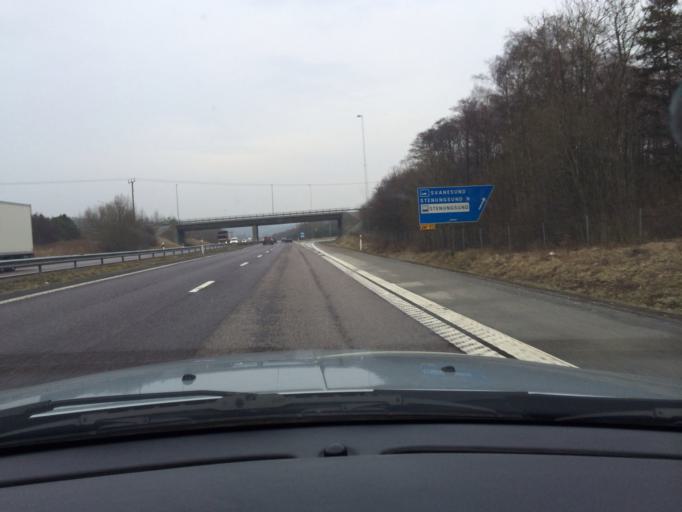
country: SE
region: Vaestra Goetaland
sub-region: Stenungsunds Kommun
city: Stora Hoga
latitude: 58.0555
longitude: 11.8761
